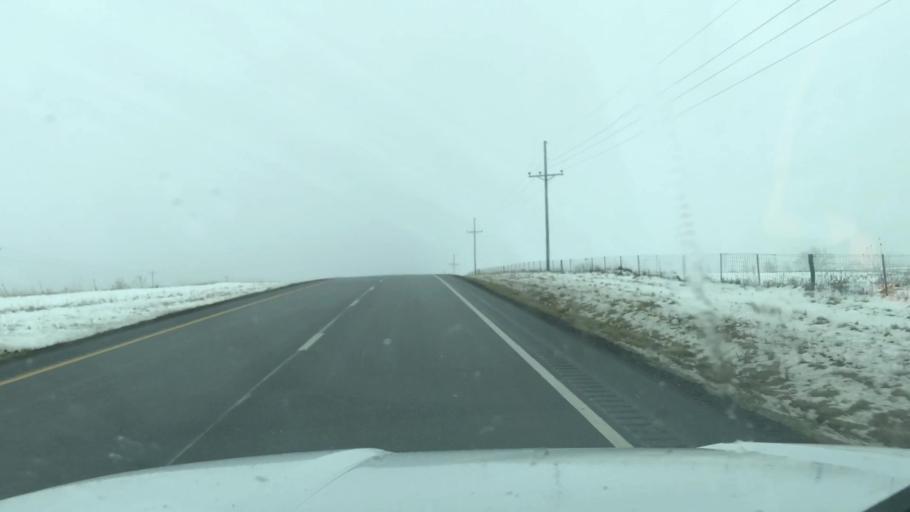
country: US
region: Missouri
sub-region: Clinton County
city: Cameron
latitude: 39.7538
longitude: -94.2757
